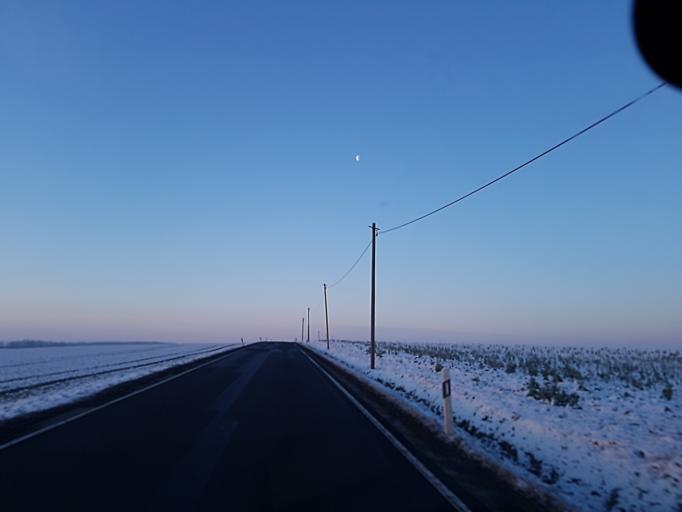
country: DE
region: Saxony
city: Oschatz
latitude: 51.2777
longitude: 13.1261
